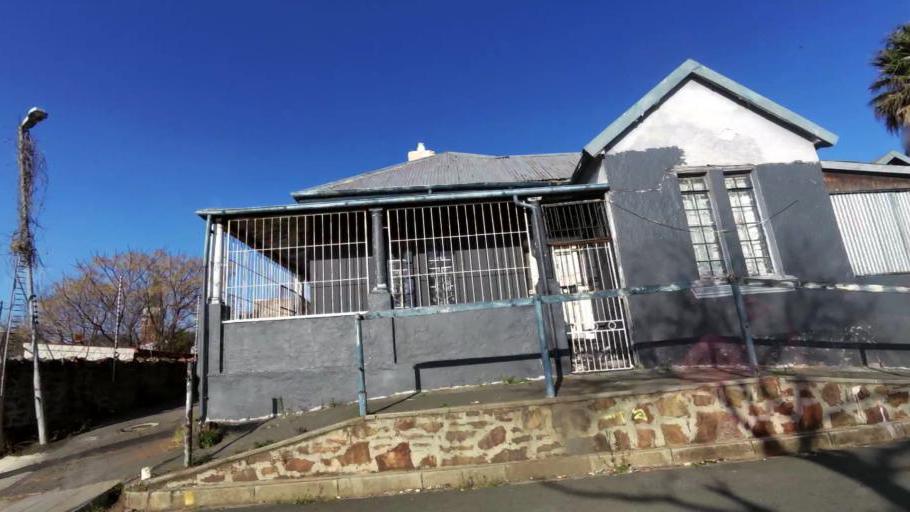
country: ZA
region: Gauteng
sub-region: City of Johannesburg Metropolitan Municipality
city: Johannesburg
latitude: -26.1909
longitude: 27.9992
